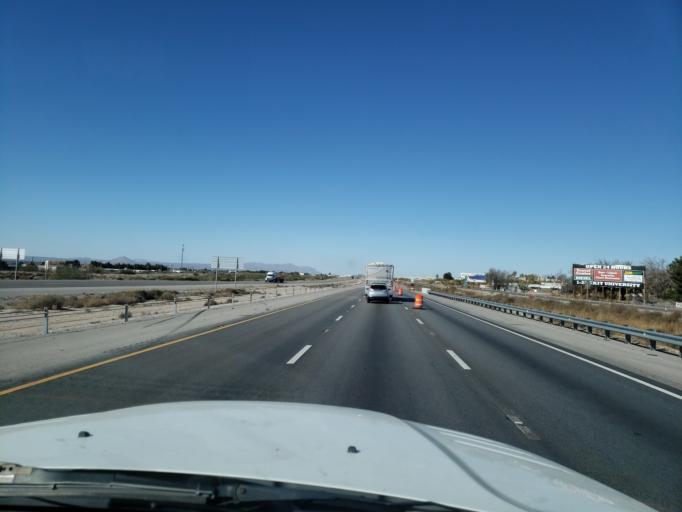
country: US
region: New Mexico
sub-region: Dona Ana County
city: University Park
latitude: 32.2503
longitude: -106.7245
